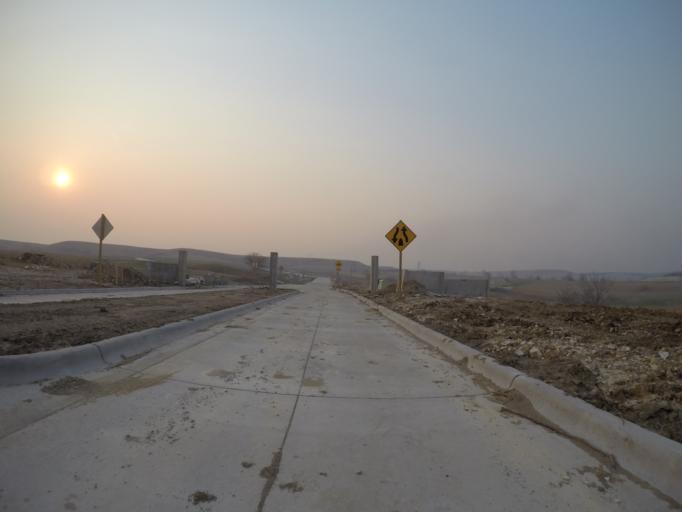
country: US
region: Kansas
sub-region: Riley County
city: Manhattan
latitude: 39.2198
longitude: -96.6415
